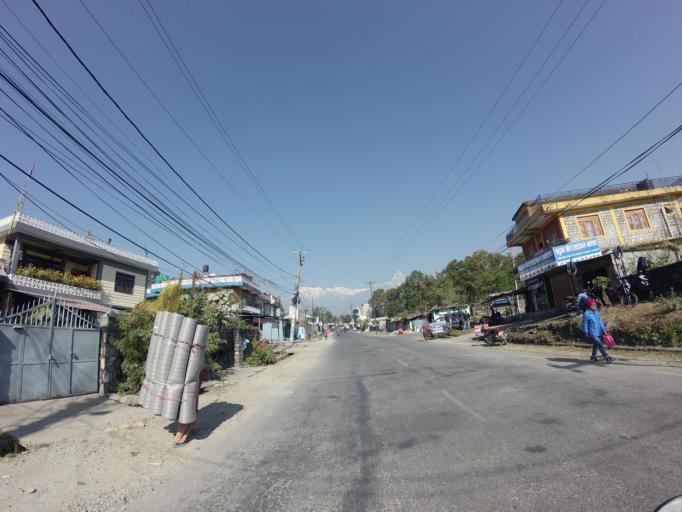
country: NP
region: Western Region
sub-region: Gandaki Zone
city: Pokhara
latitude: 28.2107
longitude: 84.0004
